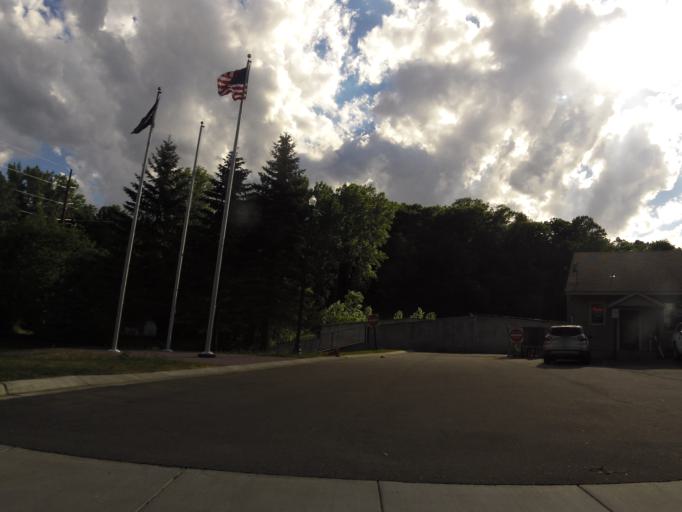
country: US
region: Minnesota
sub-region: Carver County
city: Chaska
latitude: 44.7900
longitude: -93.6066
